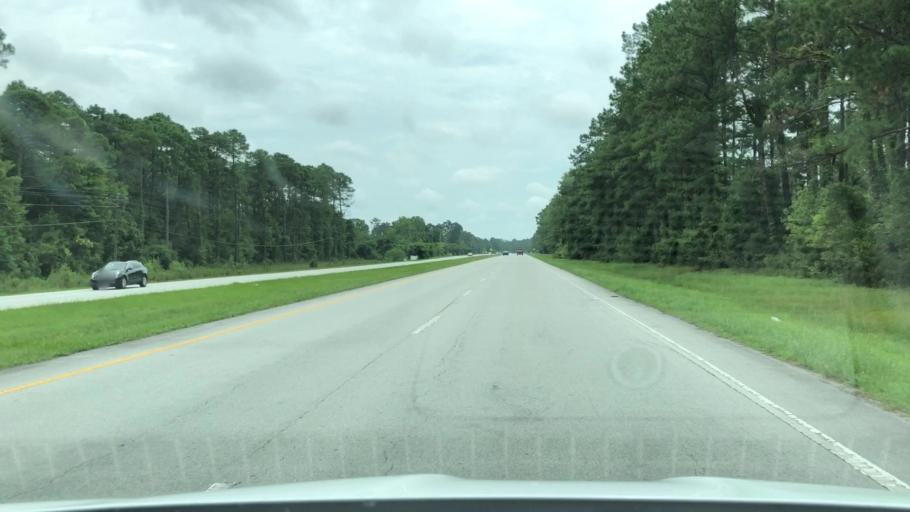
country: US
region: North Carolina
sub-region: Craven County
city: Havelock
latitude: 34.8341
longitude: -76.8810
